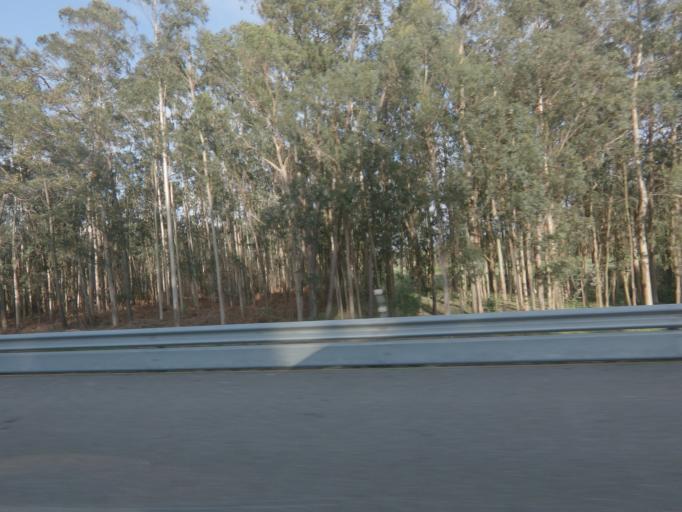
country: PT
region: Aveiro
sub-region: Ovar
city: Valega
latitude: 40.8294
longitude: -8.5542
